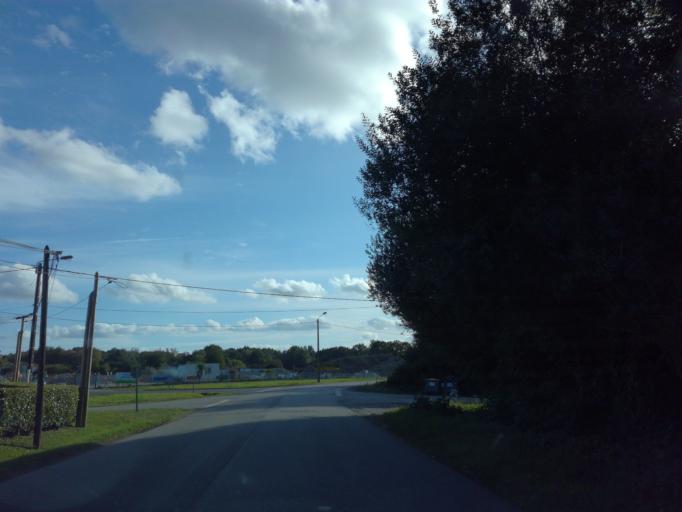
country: FR
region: Brittany
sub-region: Departement du Morbihan
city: Le Sourn
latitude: 48.0384
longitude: -2.9655
